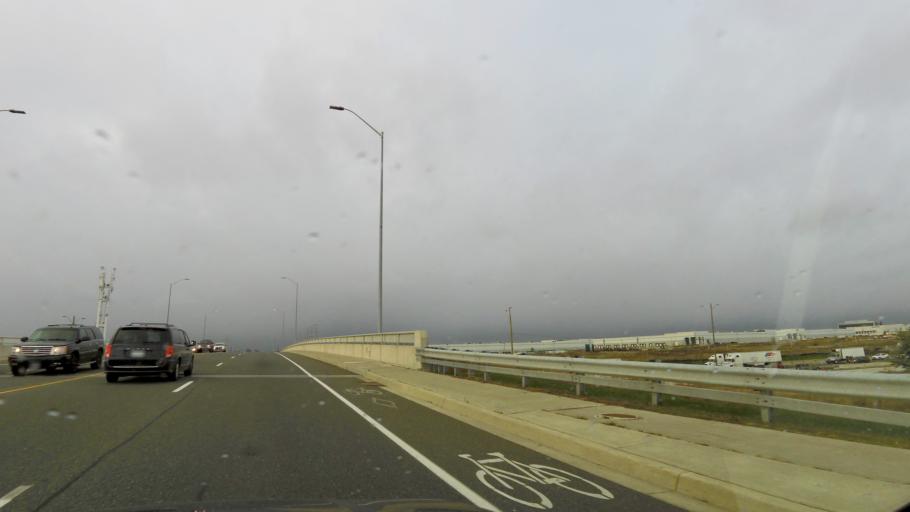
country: CA
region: Ontario
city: Mississauga
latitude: 43.6231
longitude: -79.6986
